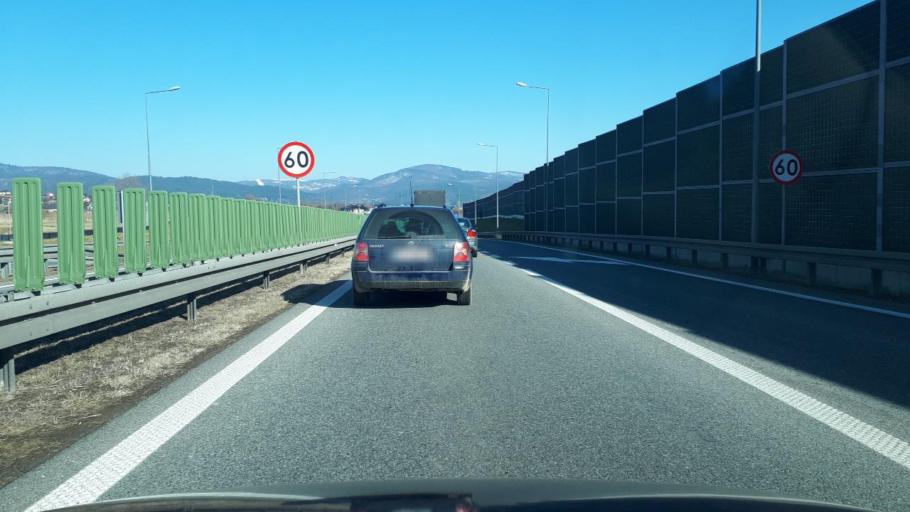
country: PL
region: Silesian Voivodeship
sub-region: Powiat zywiecki
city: Pietrzykowice
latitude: 49.6832
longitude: 19.1709
